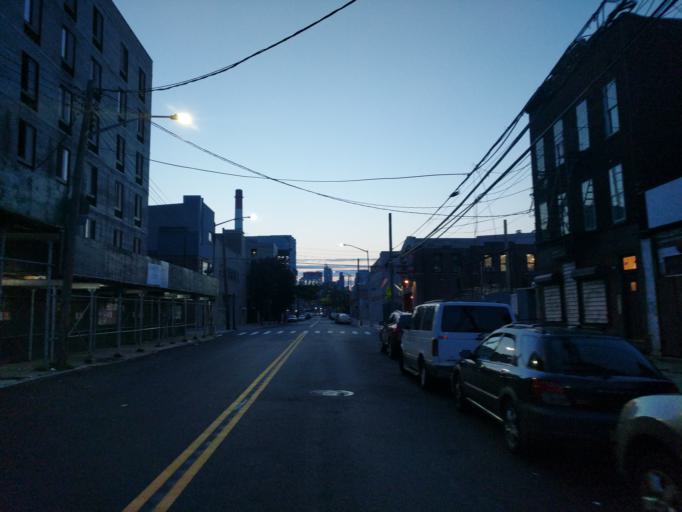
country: US
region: New York
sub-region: Queens County
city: Long Island City
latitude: 40.7593
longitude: -73.9395
